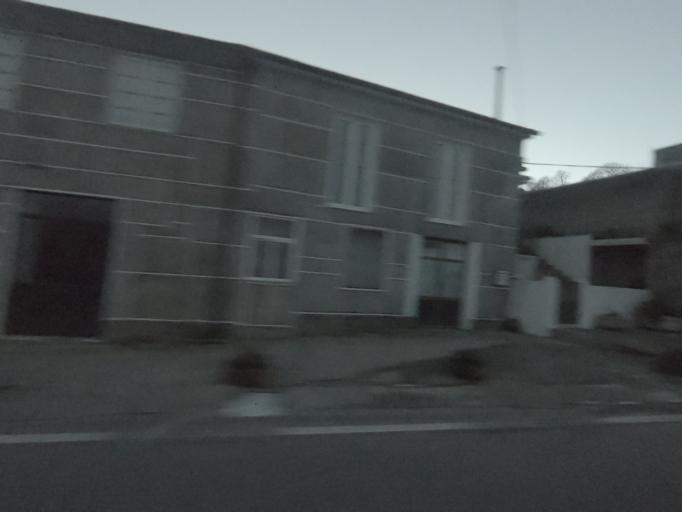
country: PT
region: Porto
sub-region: Baiao
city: Valadares
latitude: 41.1885
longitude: -7.9421
